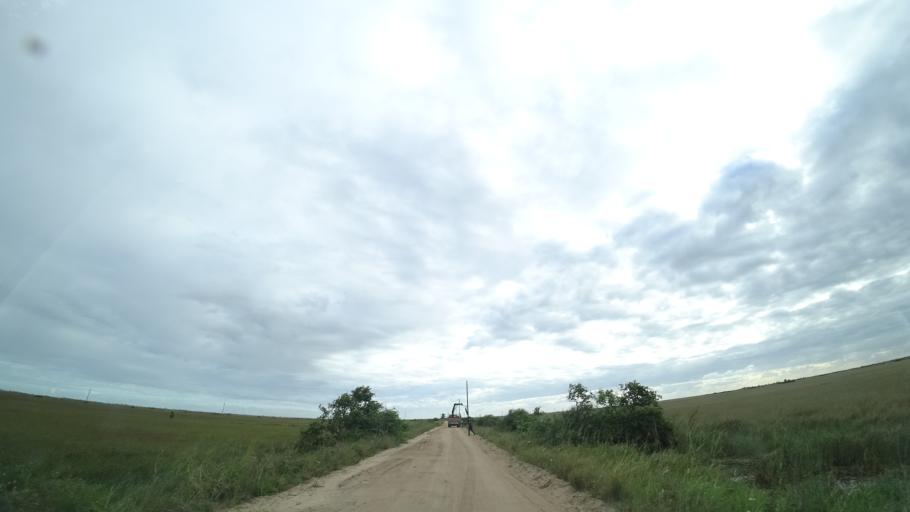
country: MZ
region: Sofala
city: Beira
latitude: -19.7419
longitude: 34.9605
